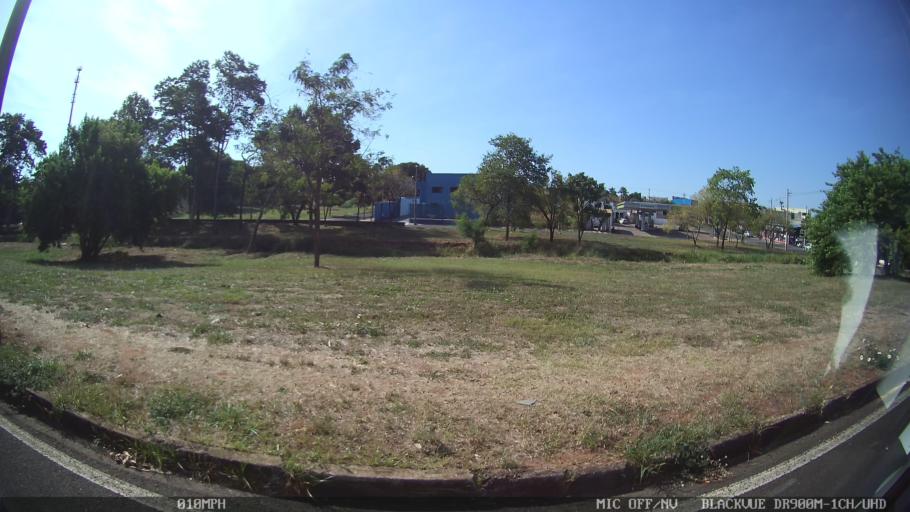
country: BR
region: Sao Paulo
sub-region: Sao Jose Do Rio Preto
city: Sao Jose do Rio Preto
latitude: -20.7924
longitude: -49.4061
